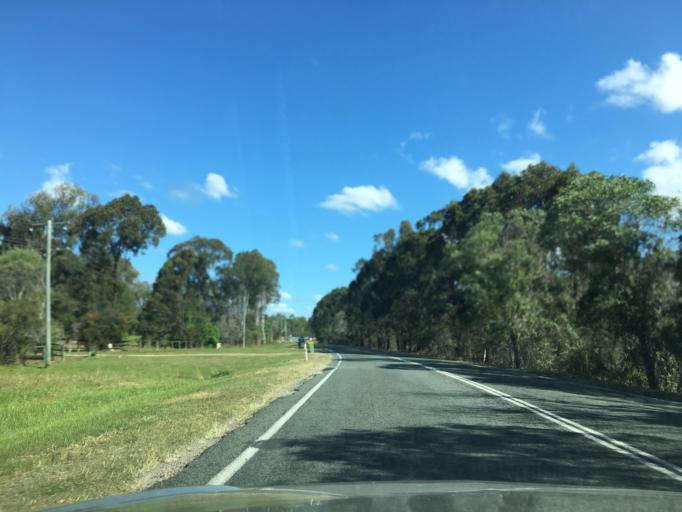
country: AU
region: Queensland
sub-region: Logan
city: Waterford West
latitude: -27.7268
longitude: 153.1273
